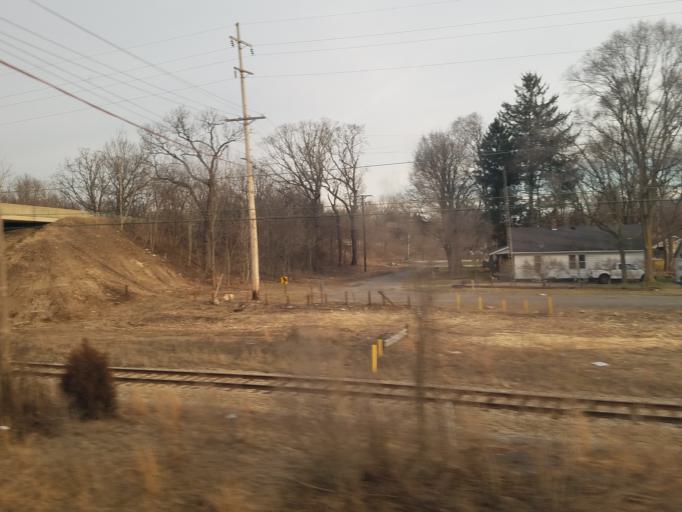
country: US
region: Indiana
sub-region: Saint Joseph County
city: South Bend
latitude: 41.6850
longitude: -86.3221
